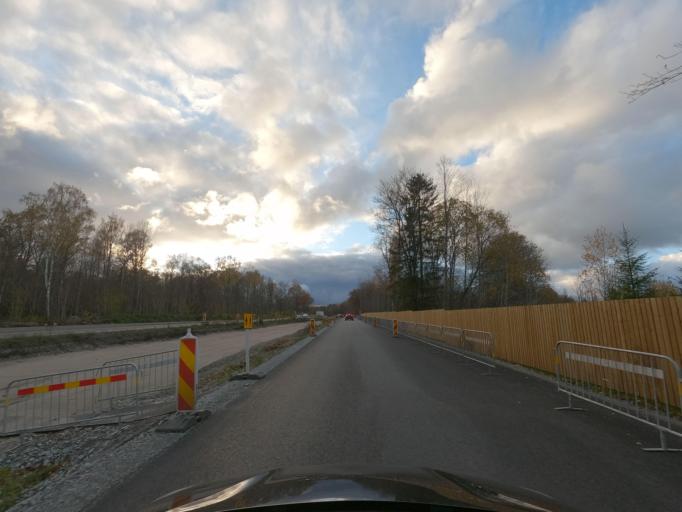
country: EE
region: Harju
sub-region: Saue linn
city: Saue
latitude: 59.3175
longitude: 24.5038
